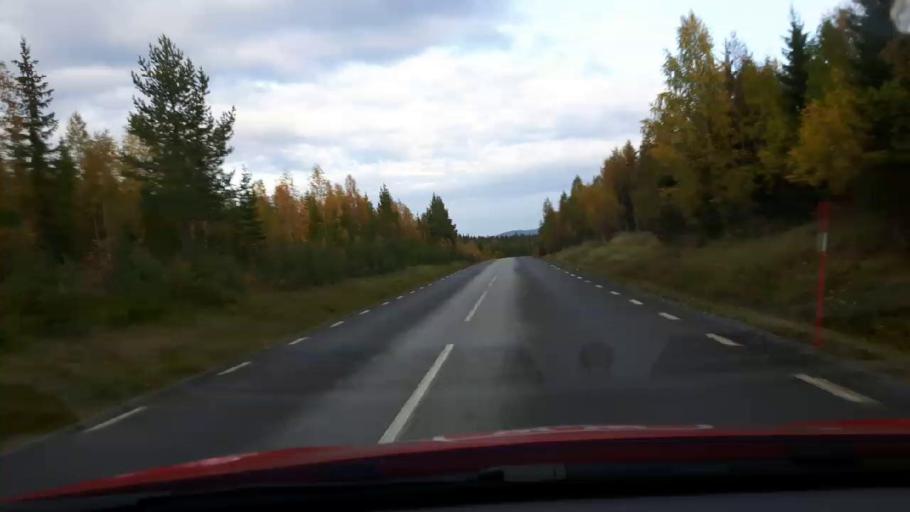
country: SE
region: Jaemtland
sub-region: OEstersunds Kommun
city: Ostersund
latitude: 63.3267
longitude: 14.6183
